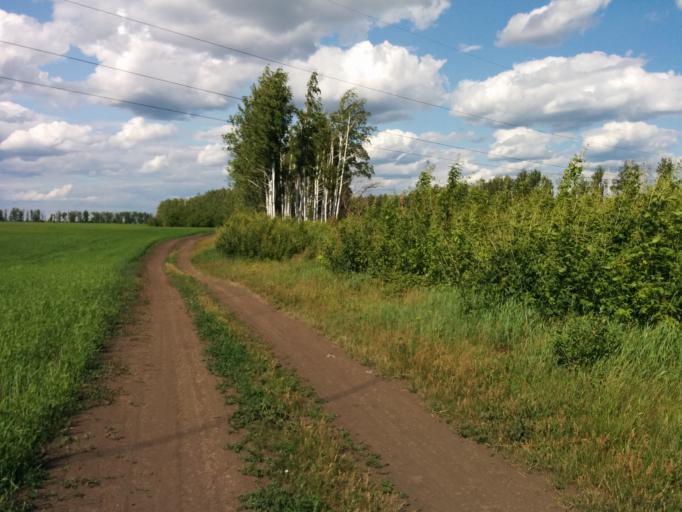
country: RU
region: Tambov
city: Tambov
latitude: 52.7971
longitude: 41.3829
